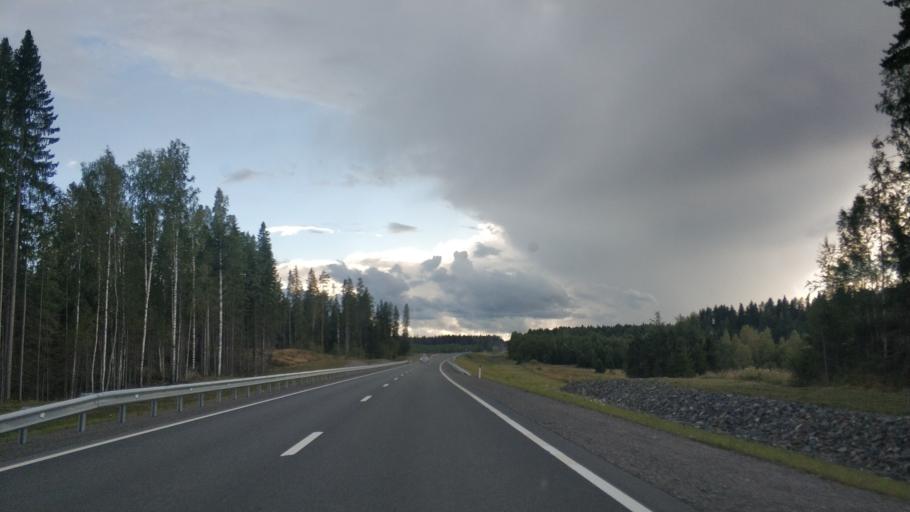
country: RU
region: Republic of Karelia
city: Lakhdenpokh'ya
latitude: 61.4498
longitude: 29.9947
